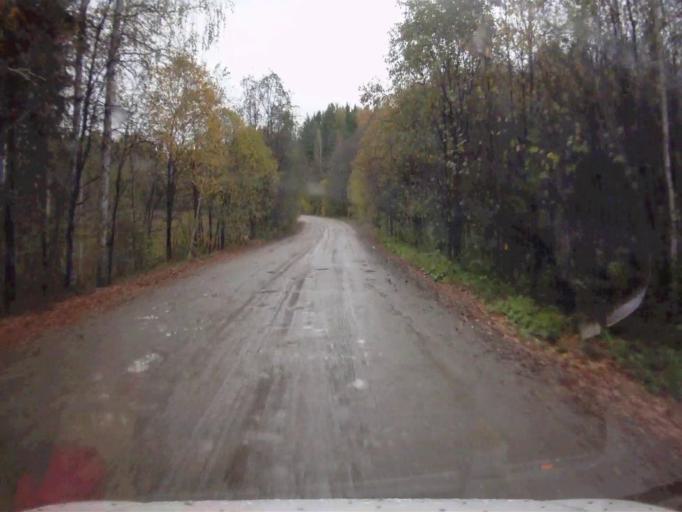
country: RU
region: Chelyabinsk
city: Kyshtym
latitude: 55.8267
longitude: 60.4865
